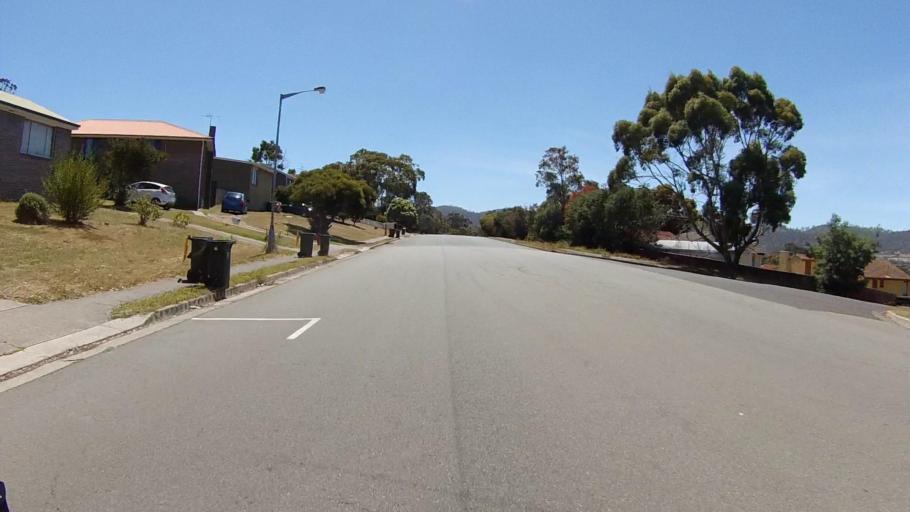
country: AU
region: Tasmania
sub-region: Clarence
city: Rokeby
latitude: -42.9022
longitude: 147.4286
